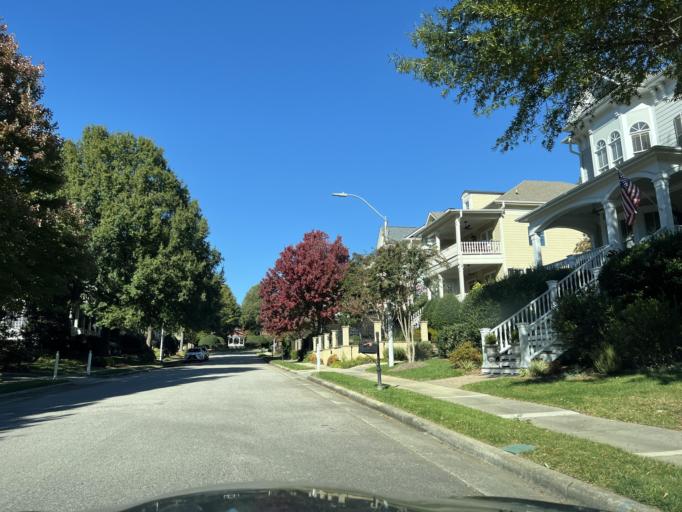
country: US
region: North Carolina
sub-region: Wake County
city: West Raleigh
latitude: 35.8935
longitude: -78.6457
